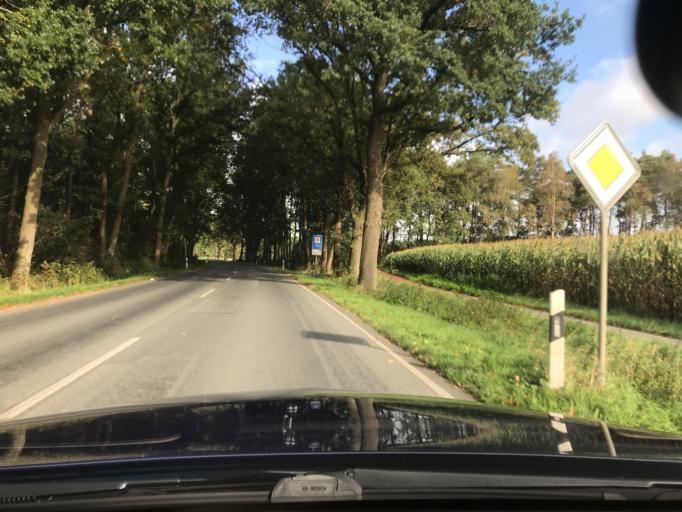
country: DE
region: Lower Saxony
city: Harsefeld
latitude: 53.4936
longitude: 9.4926
